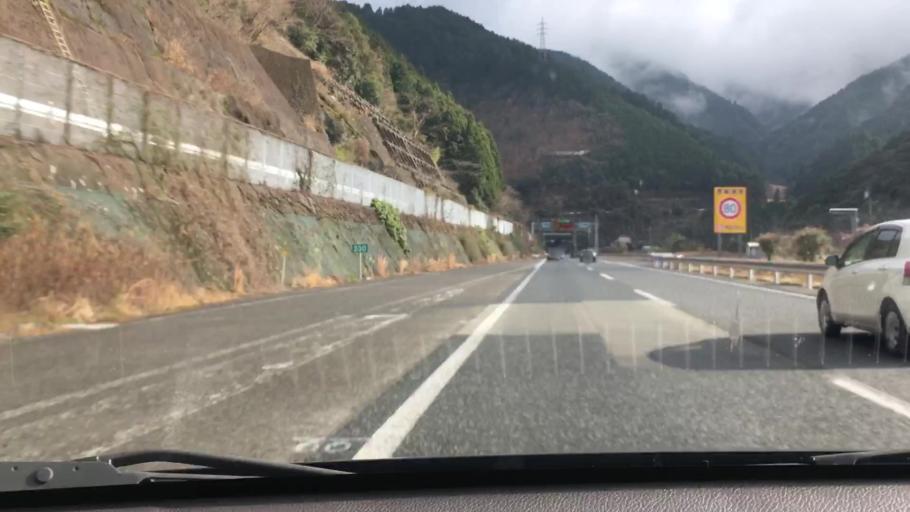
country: JP
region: Kumamoto
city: Yatsushiro
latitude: 32.3966
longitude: 130.7040
